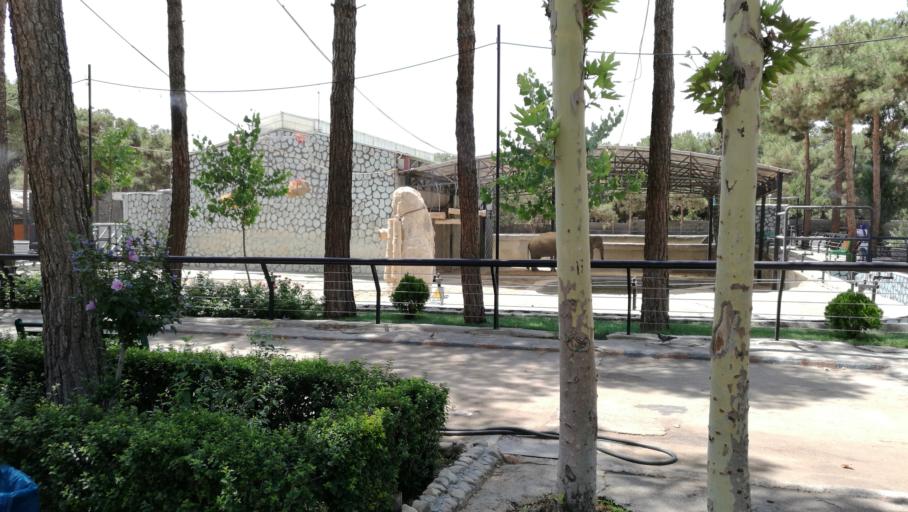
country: IR
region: Tehran
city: Tehran
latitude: 35.7191
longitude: 51.2926
